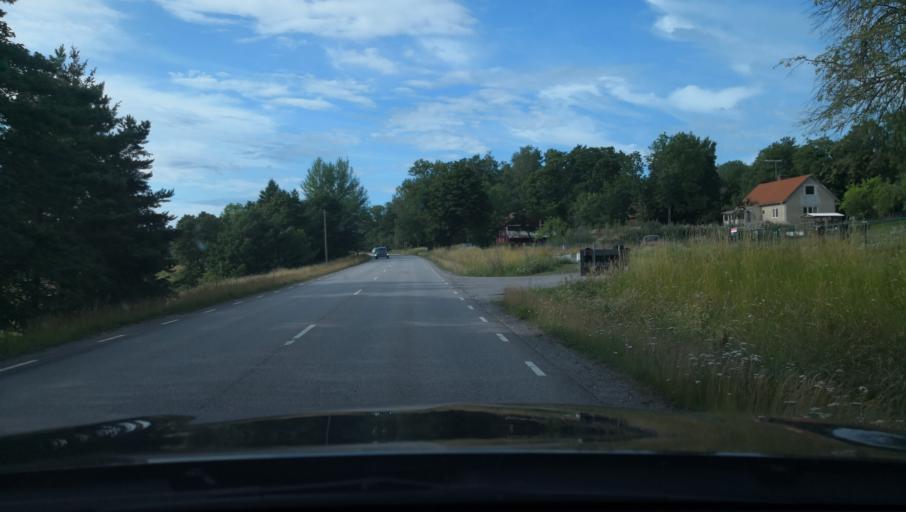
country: SE
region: Uppsala
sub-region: Habo Kommun
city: Balsta
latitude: 59.5985
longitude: 17.5091
